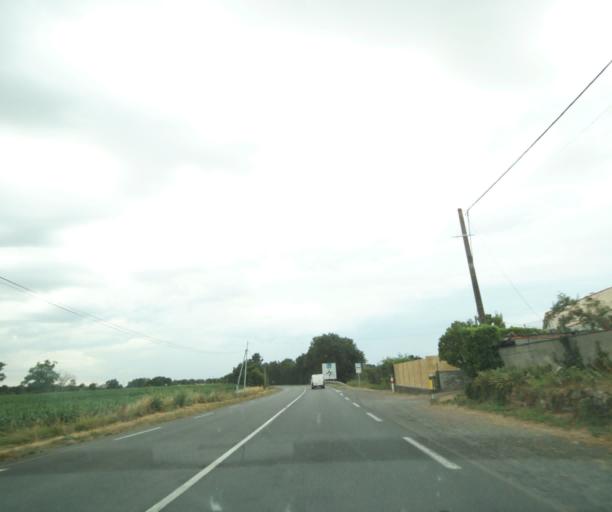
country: FR
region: Pays de la Loire
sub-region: Departement de la Vendee
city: Chaille-les-Marais
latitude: 46.4060
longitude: -1.0359
